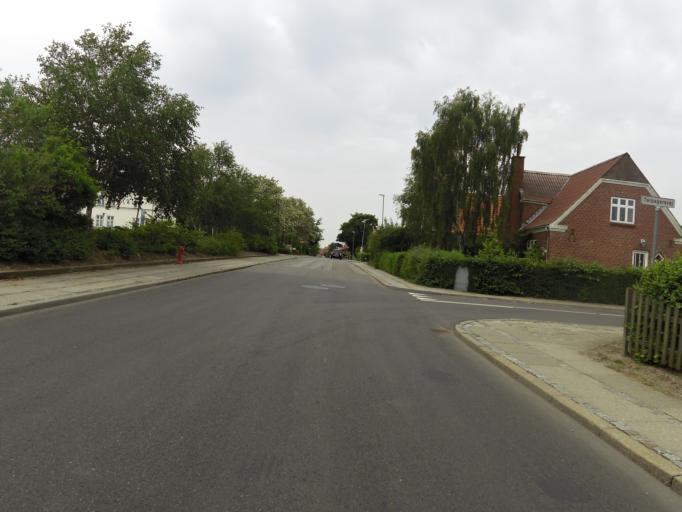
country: DK
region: South Denmark
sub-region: Esbjerg Kommune
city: Ribe
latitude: 55.3278
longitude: 8.7788
